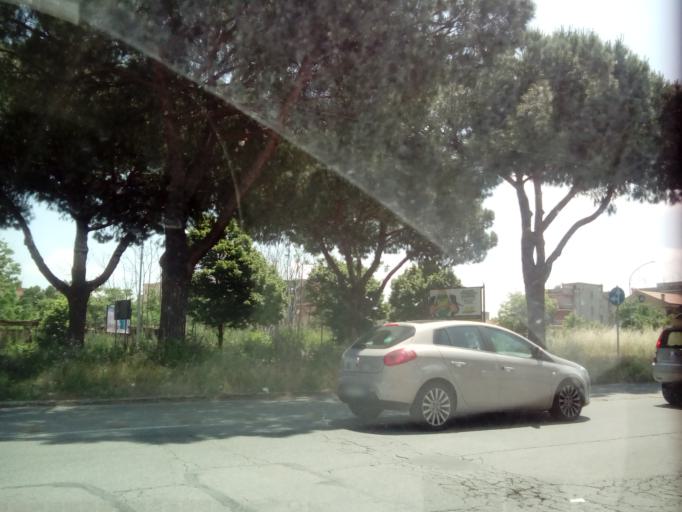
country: IT
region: Latium
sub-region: Citta metropolitana di Roma Capitale
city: Rome
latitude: 41.8824
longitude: 12.5729
